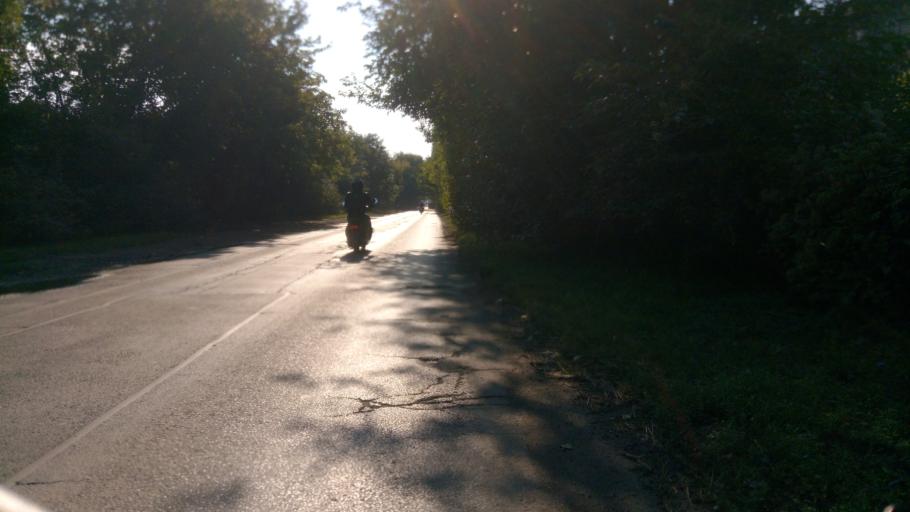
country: HU
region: Pest
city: Budaors
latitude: 47.4474
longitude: 18.9836
